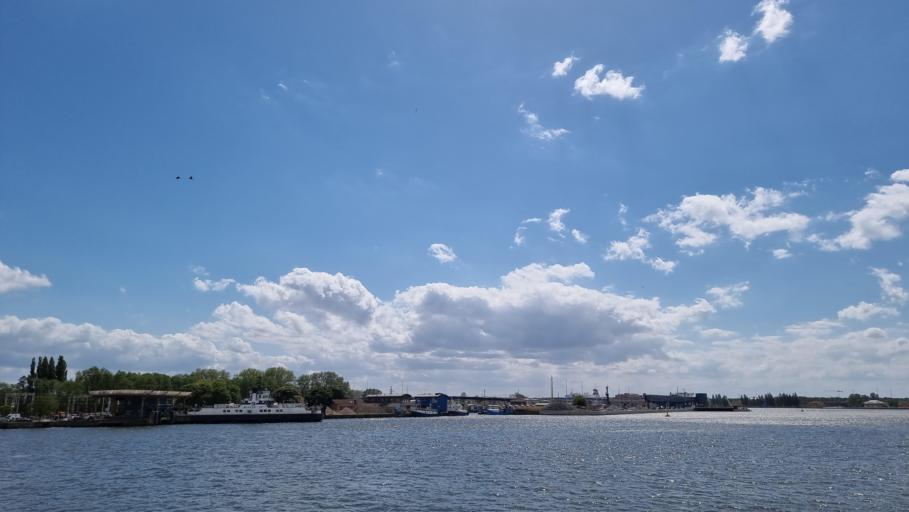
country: PL
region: West Pomeranian Voivodeship
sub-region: Swinoujscie
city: Swinoujscie
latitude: 53.9081
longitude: 14.2665
